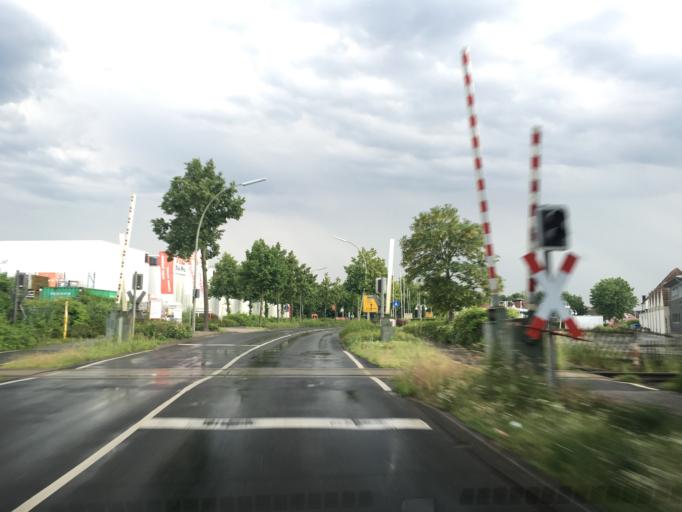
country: DE
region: North Rhine-Westphalia
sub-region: Regierungsbezirk Munster
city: Steinfurt
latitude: 52.1203
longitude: 7.3905
